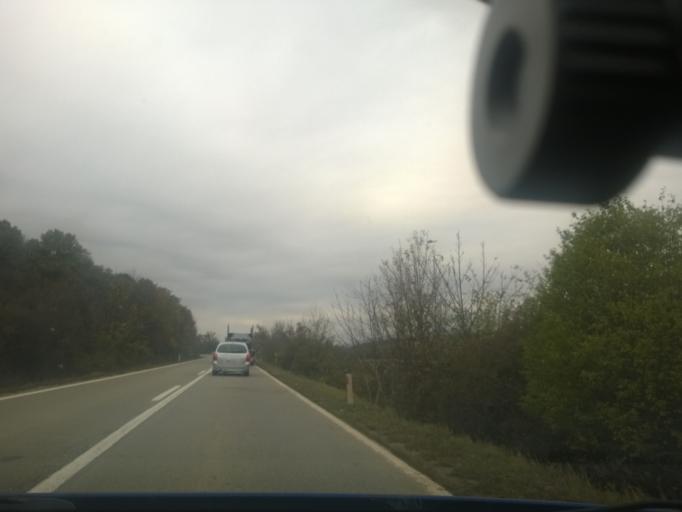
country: RS
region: Central Serbia
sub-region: Pirotski Okrug
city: Dimitrovgrad
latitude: 43.0555
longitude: 22.6943
